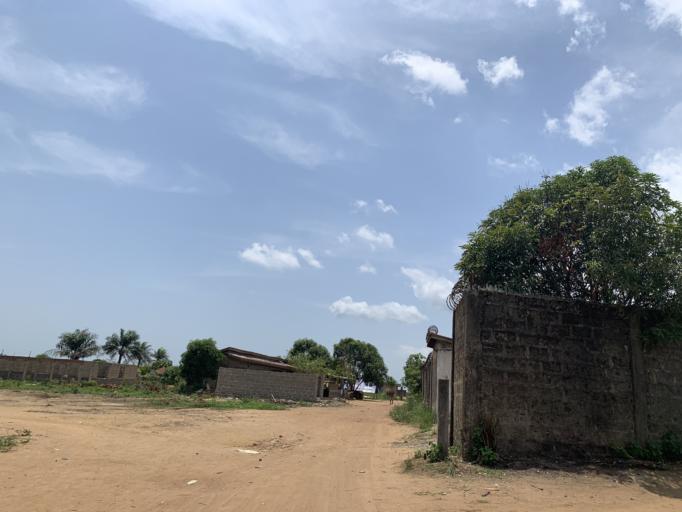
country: SL
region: Western Area
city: Waterloo
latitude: 8.3389
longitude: -13.0256
